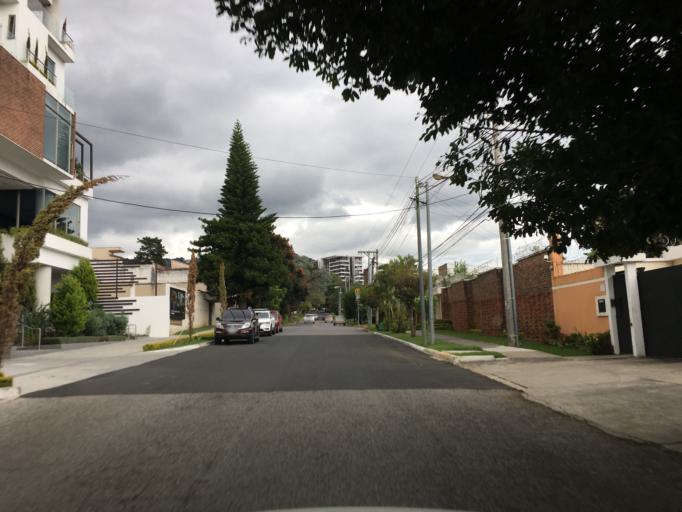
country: GT
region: Guatemala
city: Santa Catarina Pinula
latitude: 14.5888
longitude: -90.4918
